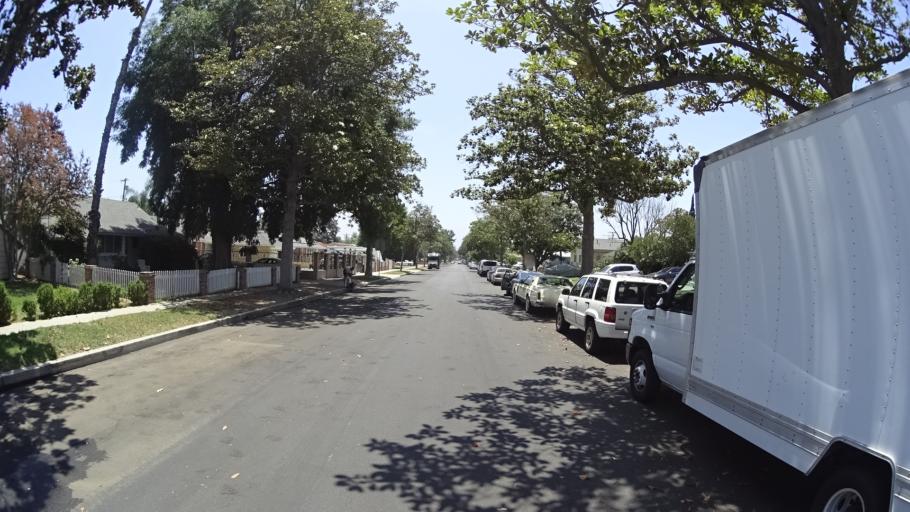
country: US
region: California
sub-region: Los Angeles County
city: Van Nuys
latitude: 34.2001
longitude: -118.4379
